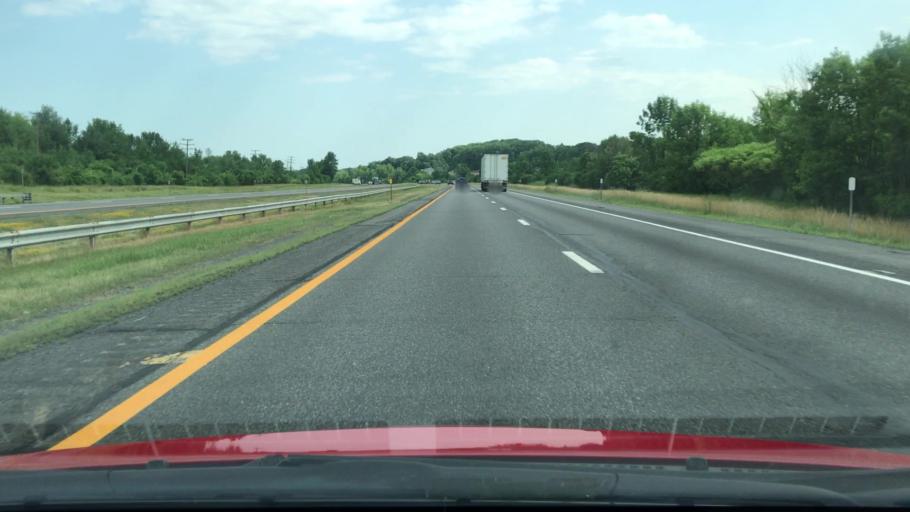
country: US
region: New York
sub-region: Albany County
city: Ravena
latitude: 42.4632
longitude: -73.8072
